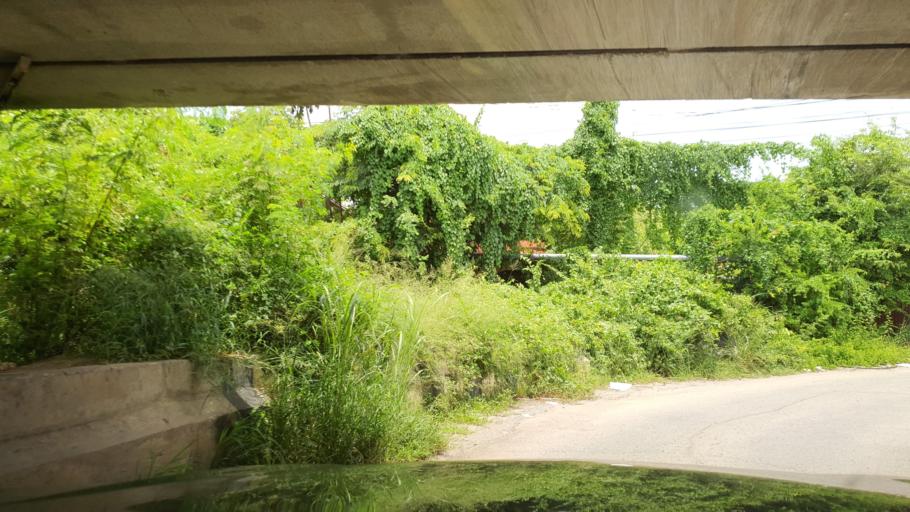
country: TH
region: Phra Nakhon Si Ayutthaya
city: Phra Nakhon Si Ayutthaya
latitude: 14.3594
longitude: 100.6123
